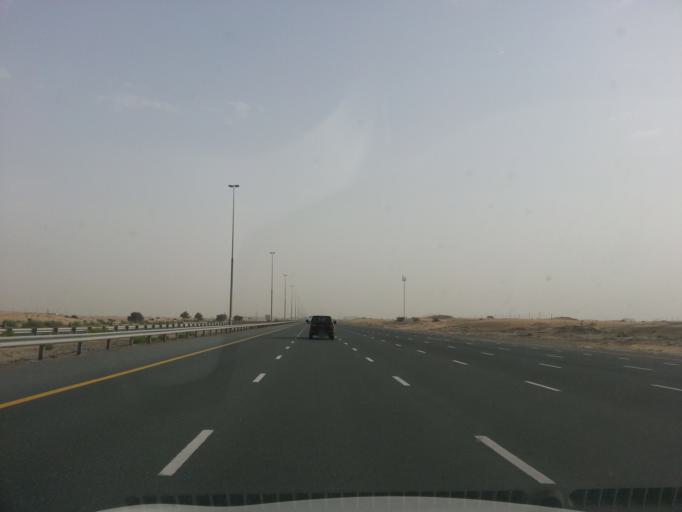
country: AE
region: Dubai
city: Dubai
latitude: 24.9740
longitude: 55.2393
